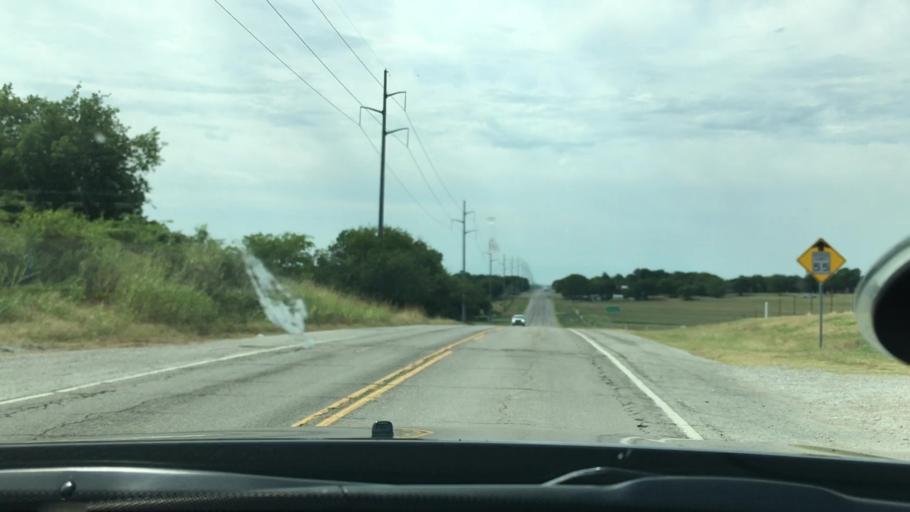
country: US
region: Oklahoma
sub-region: Carter County
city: Ardmore
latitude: 34.3209
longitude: -97.1430
